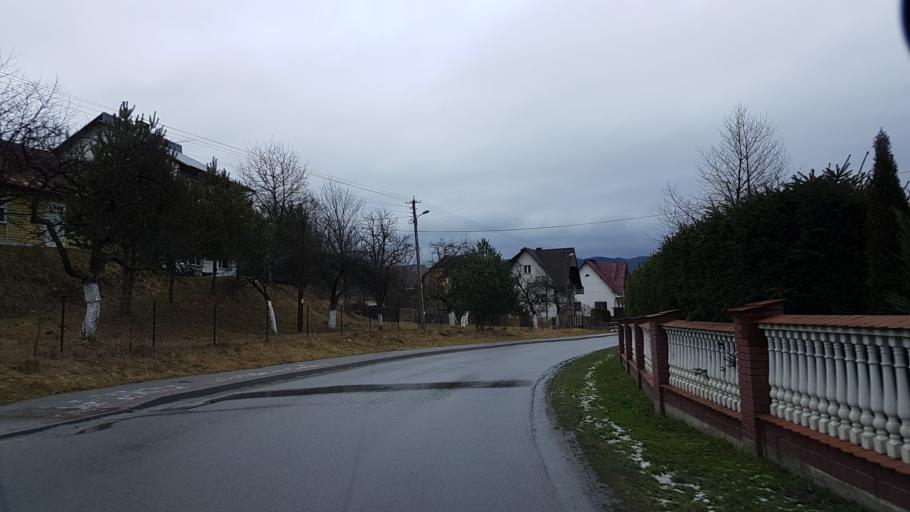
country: PL
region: Lesser Poland Voivodeship
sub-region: Powiat nowosadecki
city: Rytro
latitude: 49.5145
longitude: 20.6288
